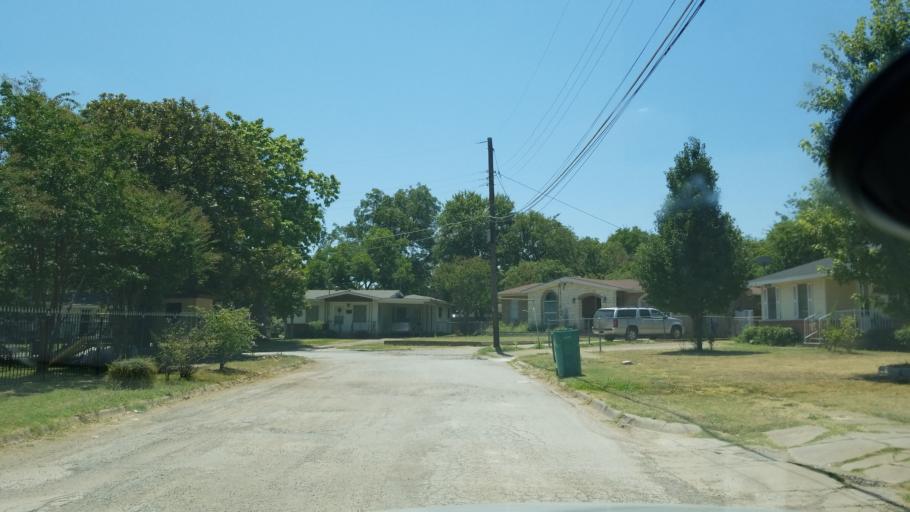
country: US
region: Texas
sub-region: Dallas County
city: Cockrell Hill
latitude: 32.7326
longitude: -96.8902
